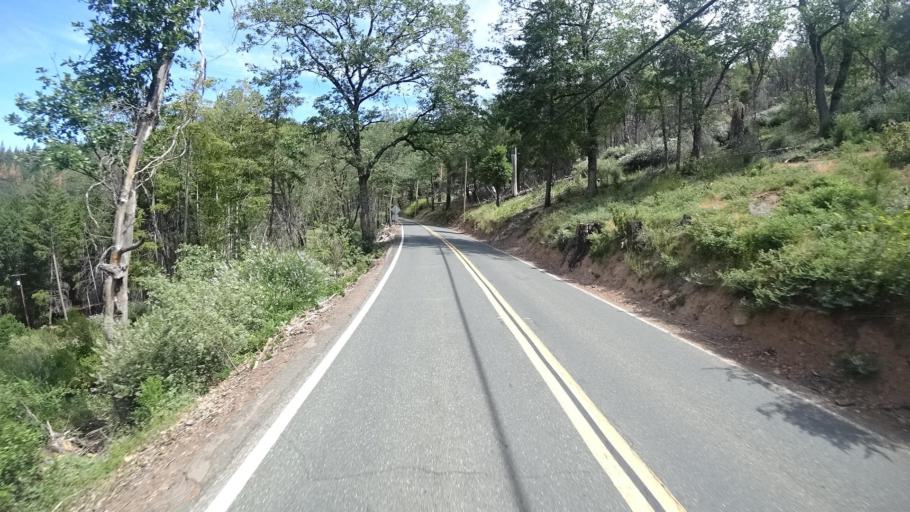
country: US
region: California
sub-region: Lake County
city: Cobb
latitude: 38.8571
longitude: -122.7062
